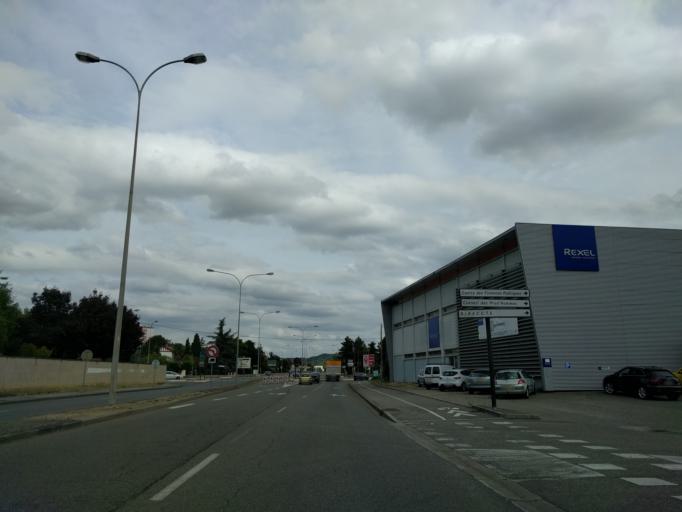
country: FR
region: Aquitaine
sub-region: Departement du Lot-et-Garonne
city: Agen
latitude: 44.1940
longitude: 0.6270
